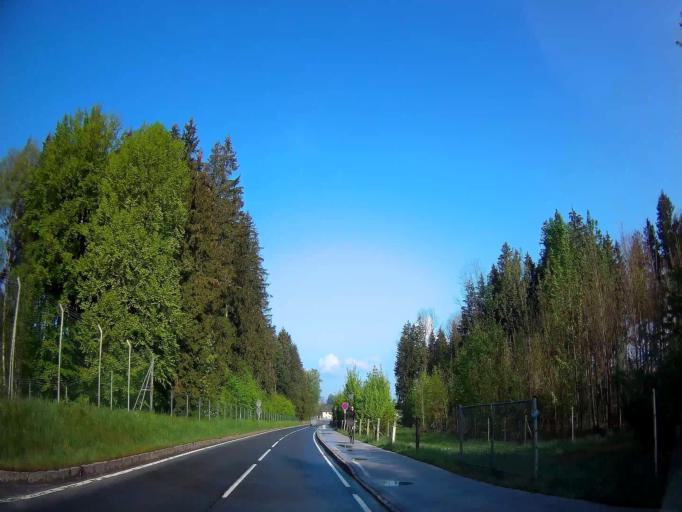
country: AT
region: Salzburg
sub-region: Politischer Bezirk Salzburg-Umgebung
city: Grodig
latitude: 47.7464
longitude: 13.0220
